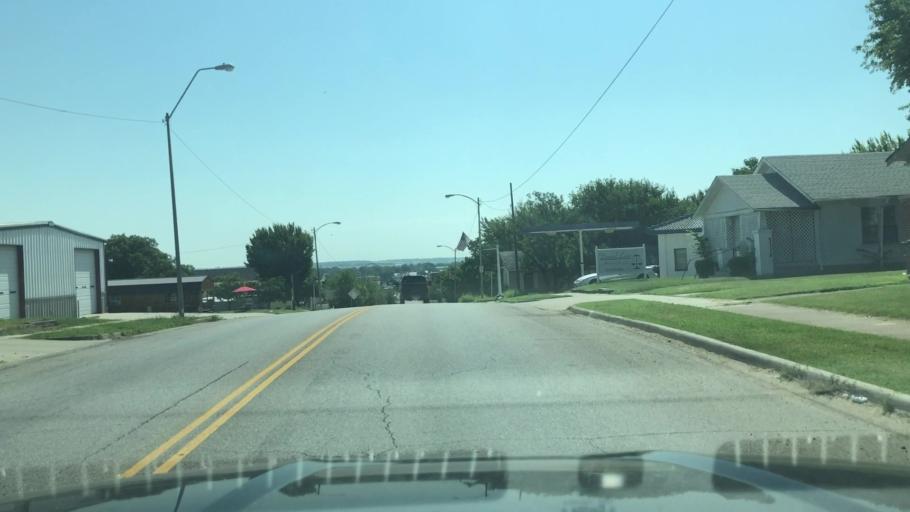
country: US
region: Oklahoma
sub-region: Creek County
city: Drumright
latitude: 35.9885
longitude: -96.6081
